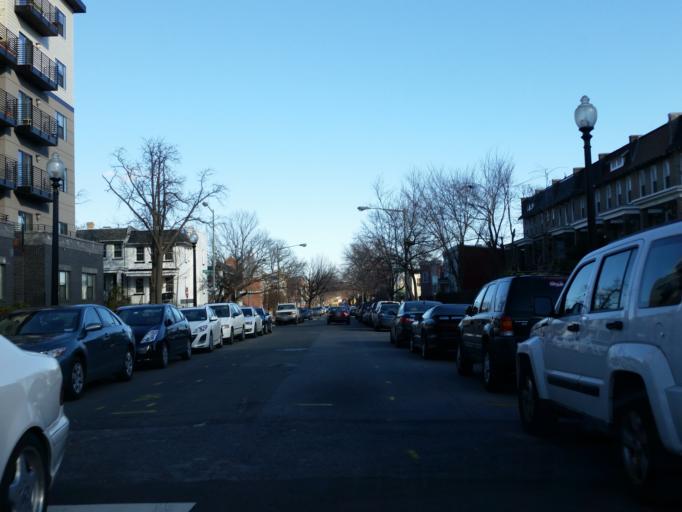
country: US
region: Washington, D.C.
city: Washington, D.C.
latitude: 38.9037
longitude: -77.0019
